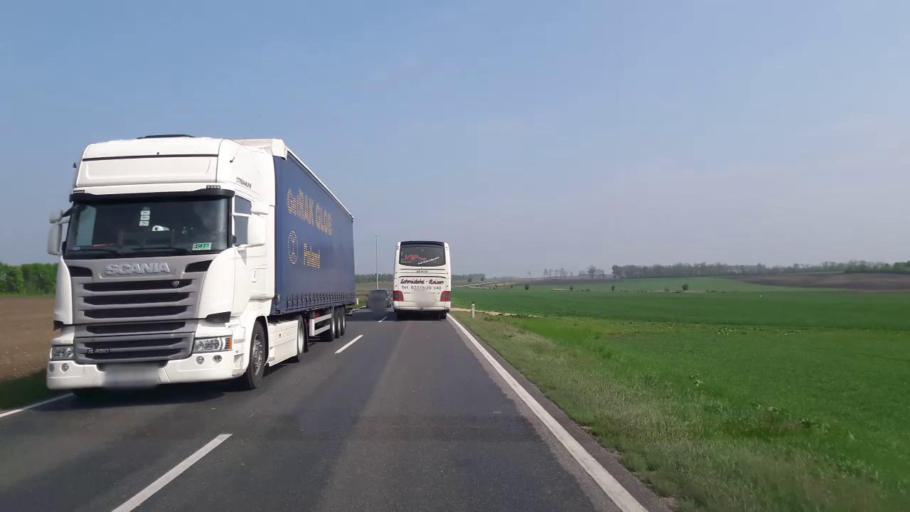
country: AT
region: Lower Austria
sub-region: Politischer Bezirk Hollabrunn
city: Guntersdorf
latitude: 48.6557
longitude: 16.0520
